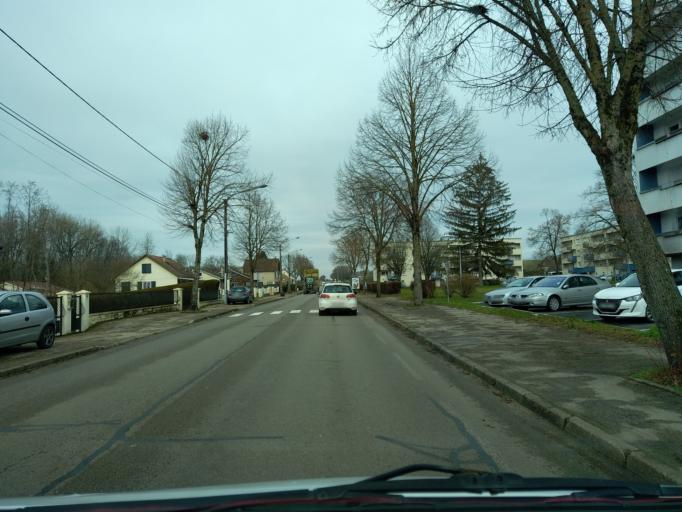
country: FR
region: Franche-Comte
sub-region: Departement de la Haute-Saone
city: Arc-les-Gray
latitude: 47.4669
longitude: 5.5819
